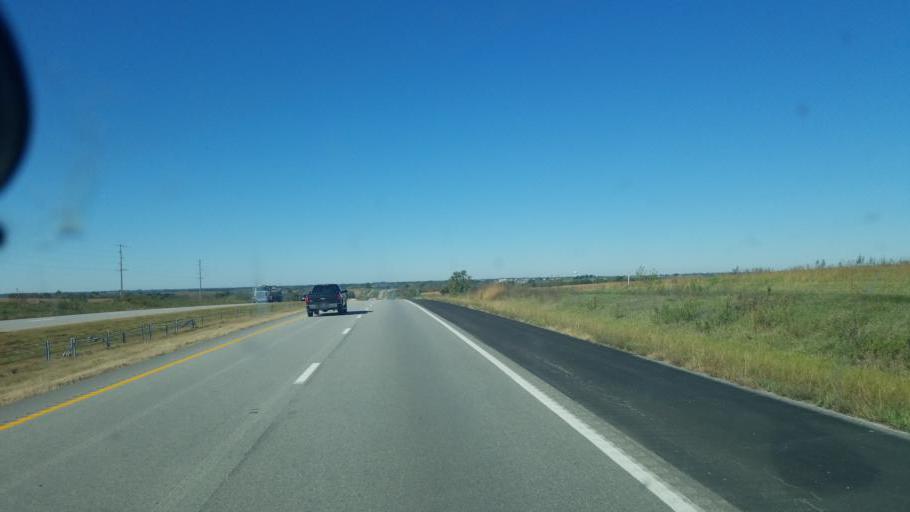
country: US
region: Missouri
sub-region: Lafayette County
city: Higginsville
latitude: 38.9925
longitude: -93.6840
